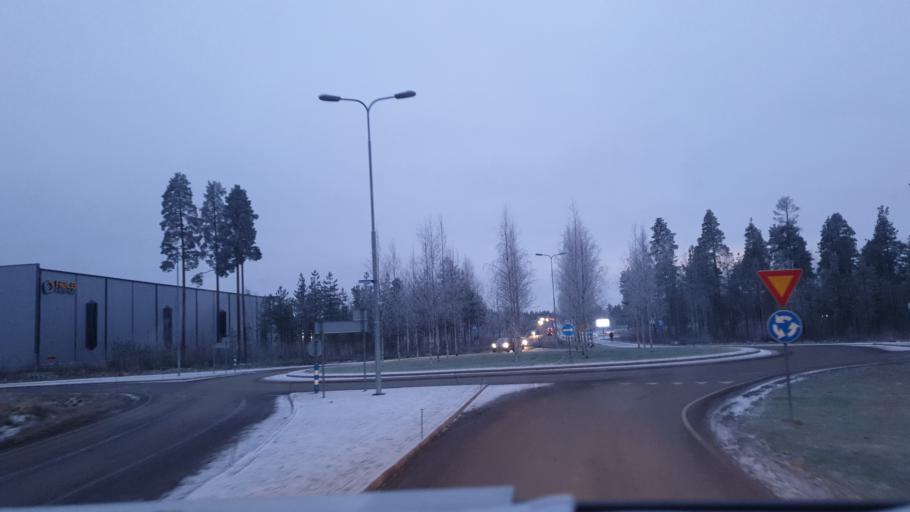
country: FI
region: Southern Ostrobothnia
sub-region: Seinaejoki
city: Nurmo
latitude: 62.7779
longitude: 22.8945
